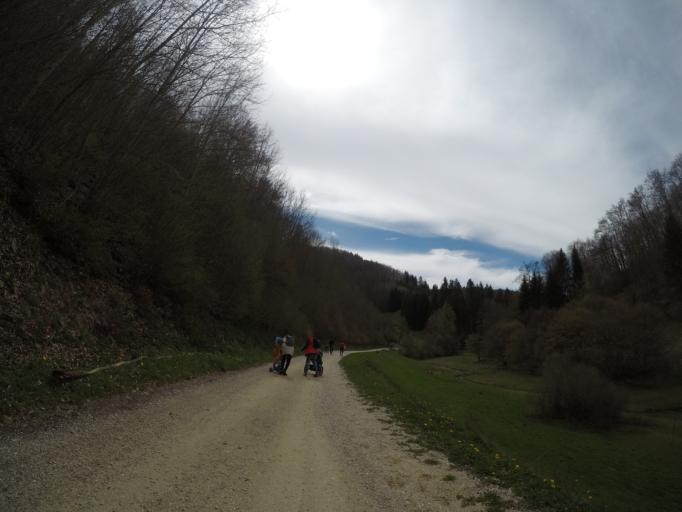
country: DE
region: Baden-Wuerttemberg
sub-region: Regierungsbezirk Stuttgart
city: Wiesensteig
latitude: 48.5535
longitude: 9.6028
